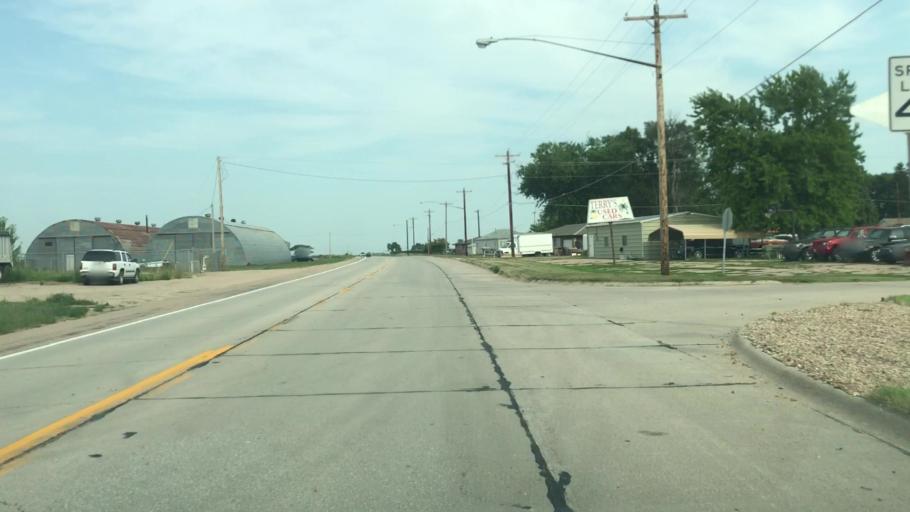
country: US
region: Nebraska
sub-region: Hall County
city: Wood River
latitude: 41.0012
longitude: -98.6048
